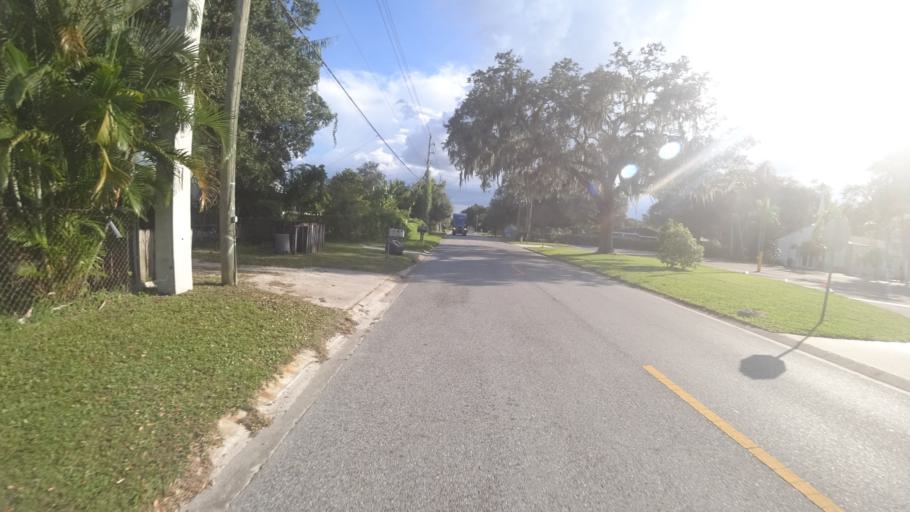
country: US
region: Florida
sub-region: Manatee County
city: Samoset
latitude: 27.4679
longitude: -82.5056
